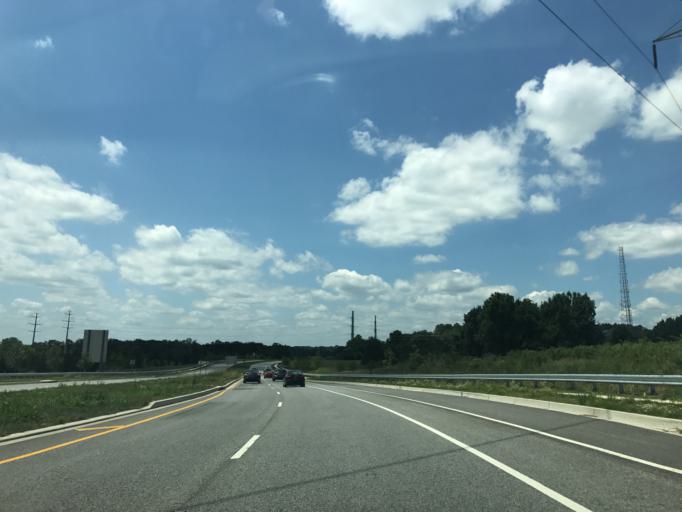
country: US
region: Maryland
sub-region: Prince George's County
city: West Laurel
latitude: 39.0870
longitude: -76.9018
